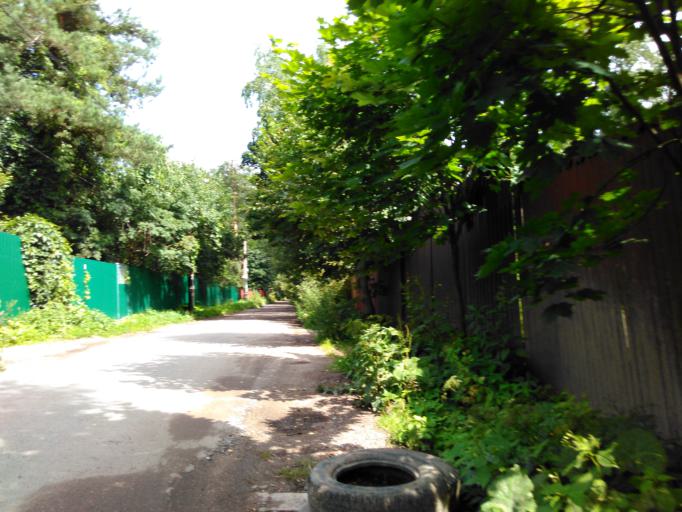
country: RU
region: Moskovskaya
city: Pravdinskiy
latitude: 56.0556
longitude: 37.8415
